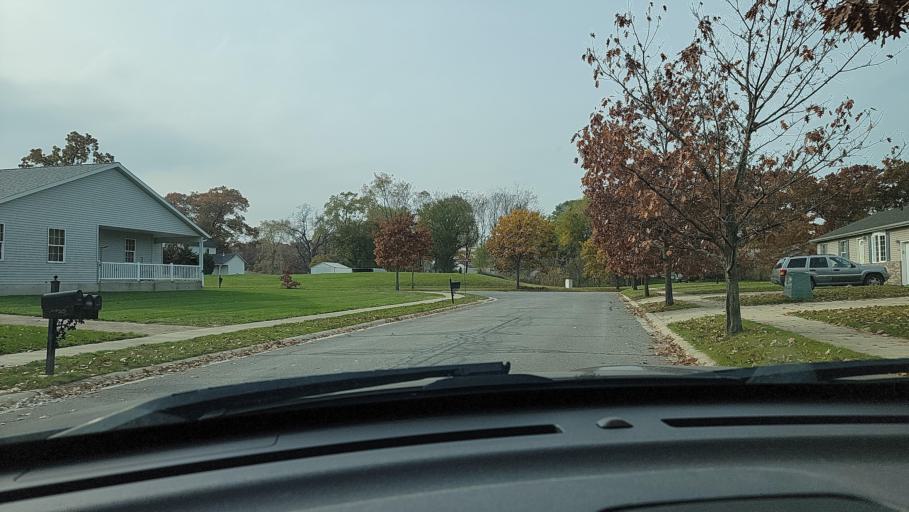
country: US
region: Indiana
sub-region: Porter County
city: Portage
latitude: 41.5876
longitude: -87.1682
